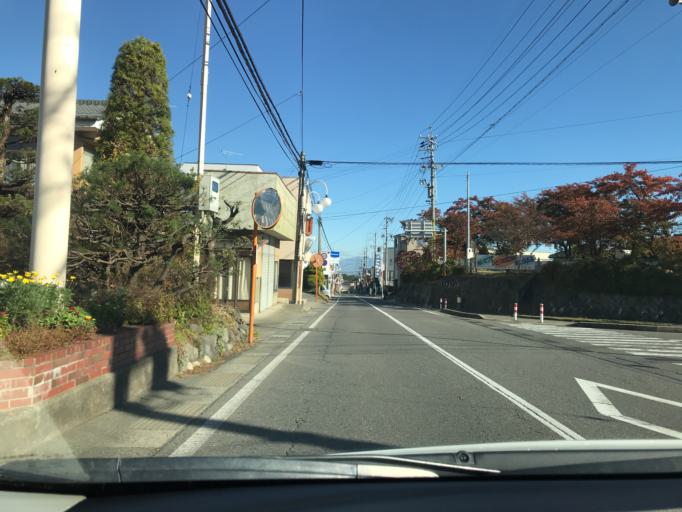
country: JP
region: Nagano
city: Toyoshina
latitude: 36.1964
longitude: 137.8547
